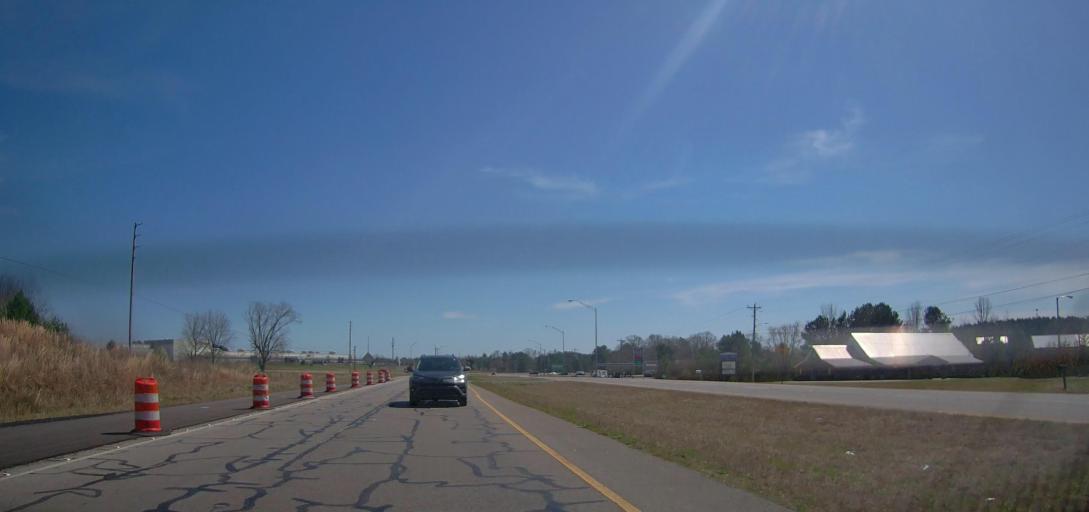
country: US
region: Alabama
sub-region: Cullman County
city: Cullman
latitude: 34.1945
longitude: -86.7881
